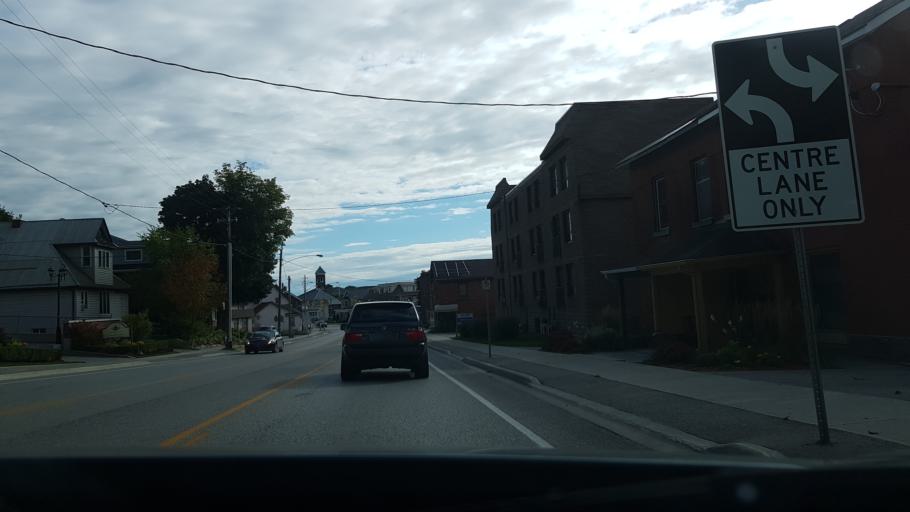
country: CA
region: Ontario
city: Orillia
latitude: 44.6094
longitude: -79.4229
